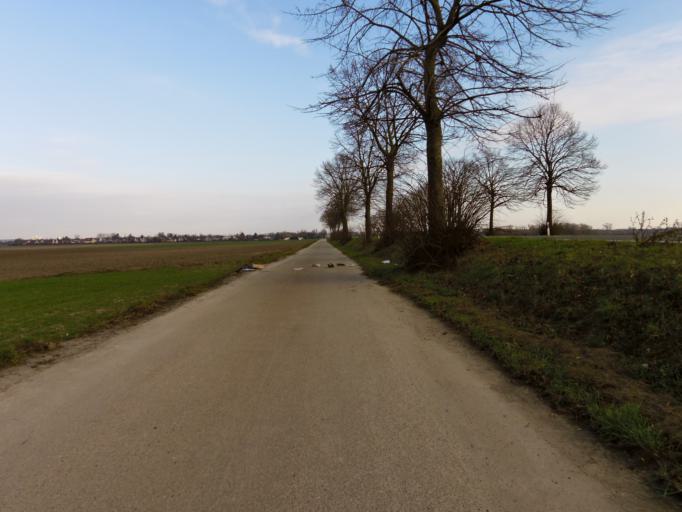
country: DE
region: Rheinland-Pfalz
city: Bobenheim-Roxheim
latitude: 49.6008
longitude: 8.3574
